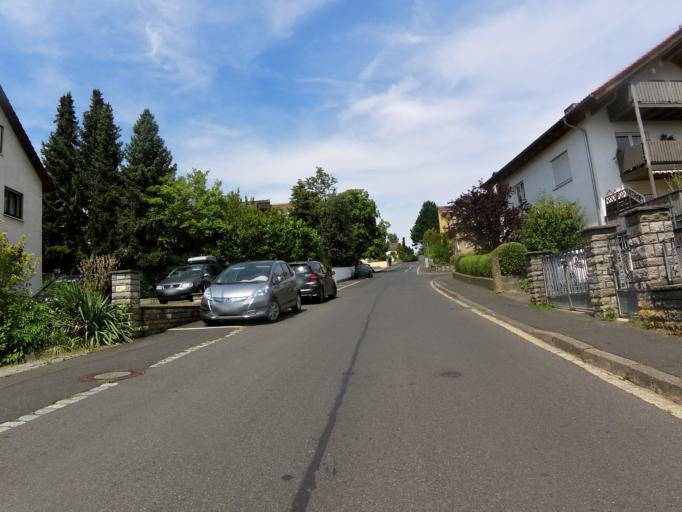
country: DE
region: Bavaria
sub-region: Regierungsbezirk Unterfranken
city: Estenfeld
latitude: 49.8125
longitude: 9.9853
